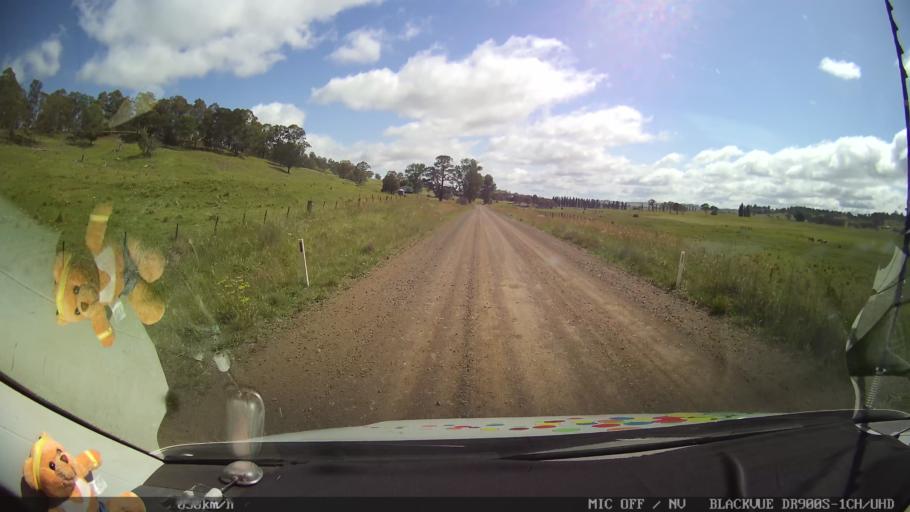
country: AU
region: New South Wales
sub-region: Glen Innes Severn
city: Glen Innes
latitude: -29.9532
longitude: 151.7054
